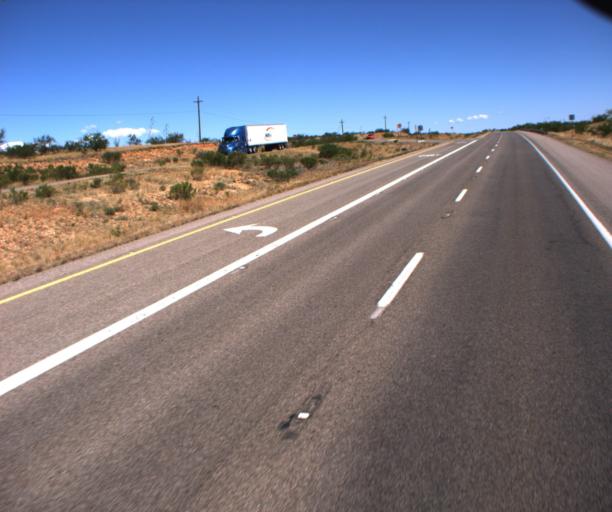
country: US
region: Arizona
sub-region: Cochise County
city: Whetstone
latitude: 31.8435
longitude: -110.3418
